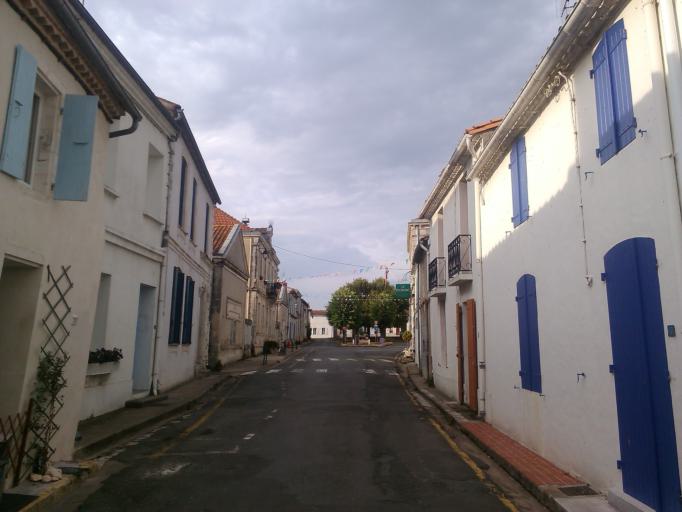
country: FR
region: Poitou-Charentes
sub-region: Departement de la Charente-Maritime
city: Breuillet
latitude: 45.7084
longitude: -1.0295
